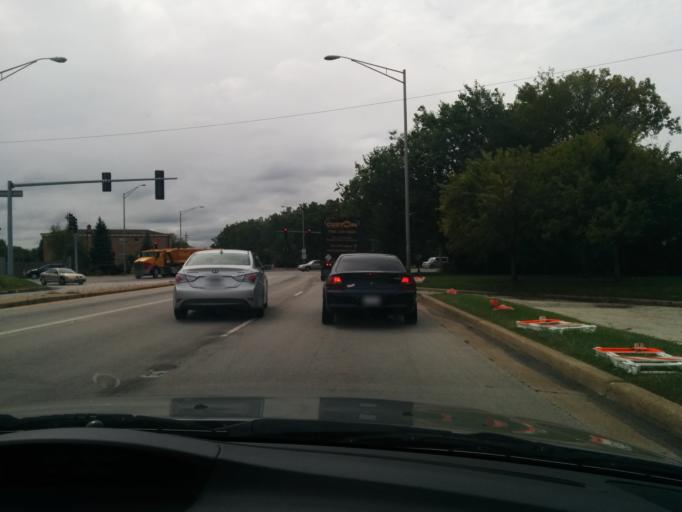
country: US
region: Illinois
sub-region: Cook County
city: North Riverside
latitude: 41.8507
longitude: -87.8229
